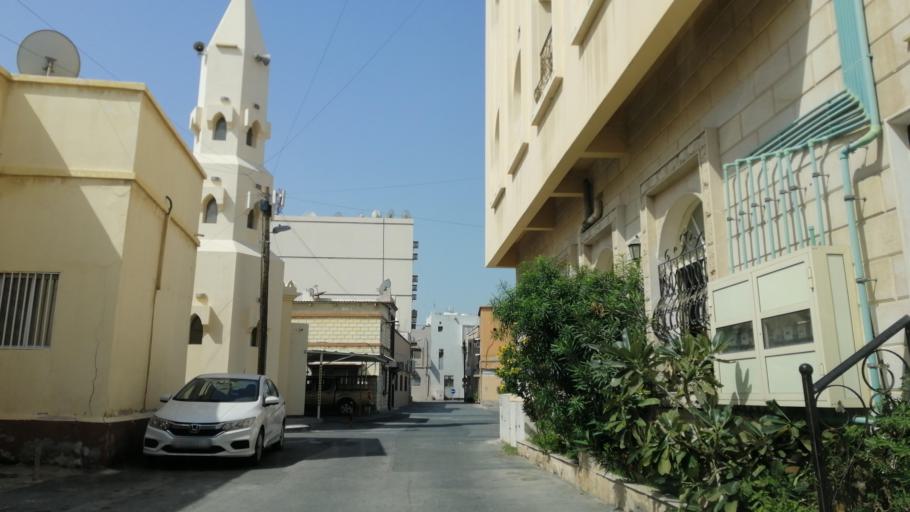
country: BH
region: Muharraq
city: Al Hadd
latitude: 26.2478
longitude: 50.6551
